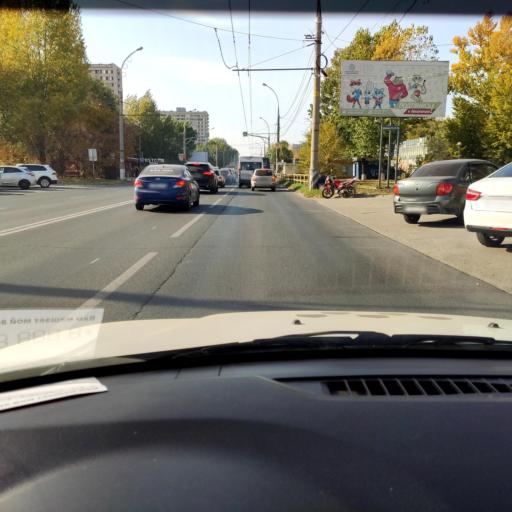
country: RU
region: Samara
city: Tol'yatti
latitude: 53.5060
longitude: 49.2843
